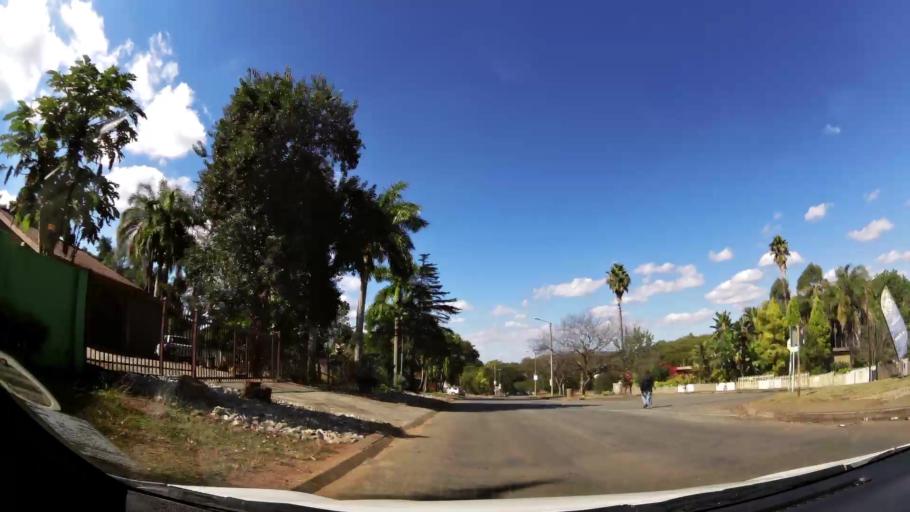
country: ZA
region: Limpopo
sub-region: Mopani District Municipality
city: Tzaneen
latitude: -23.8158
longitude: 30.1558
